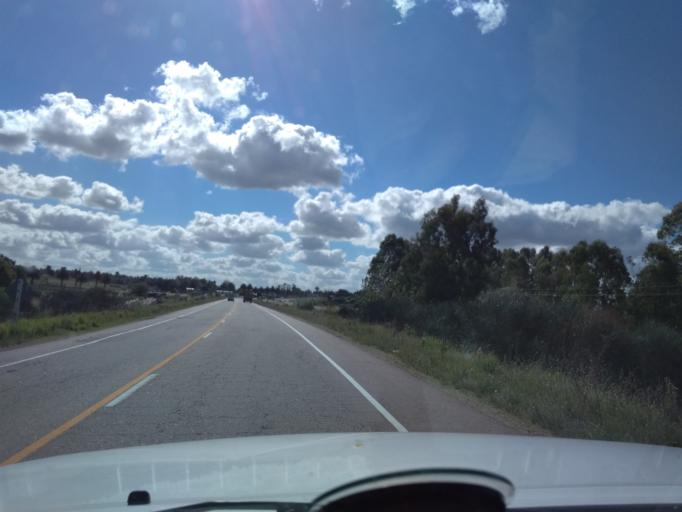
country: UY
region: Canelones
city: Sauce
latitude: -34.6724
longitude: -56.0526
